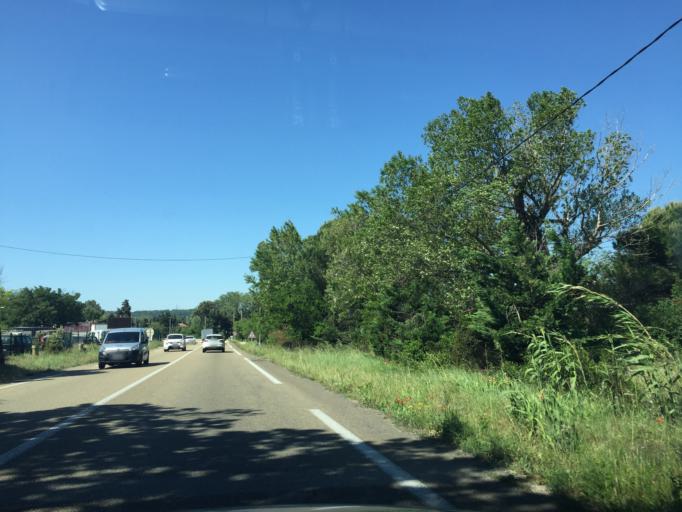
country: FR
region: Languedoc-Roussillon
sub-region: Departement du Gard
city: Rochefort-du-Gard
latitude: 43.9531
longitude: 4.7143
